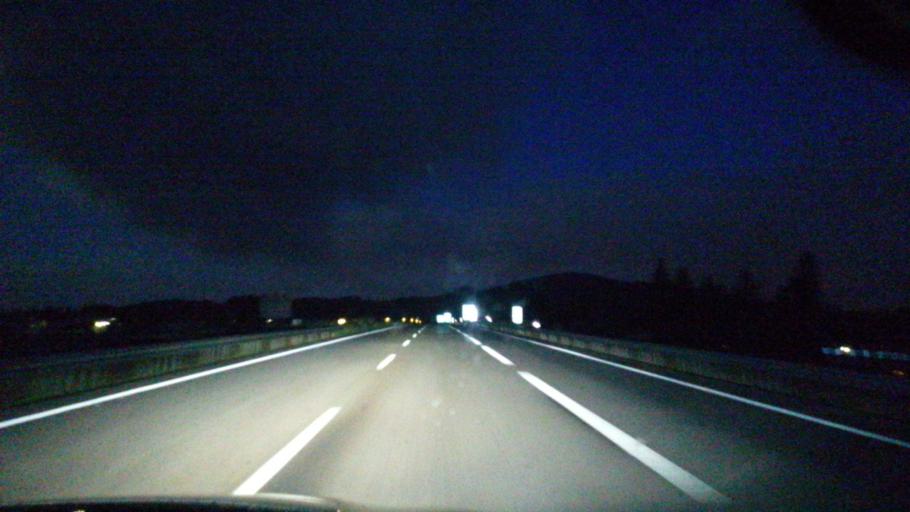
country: PT
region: Porto
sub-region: Lousada
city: Lousada
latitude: 41.2866
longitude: -8.2594
